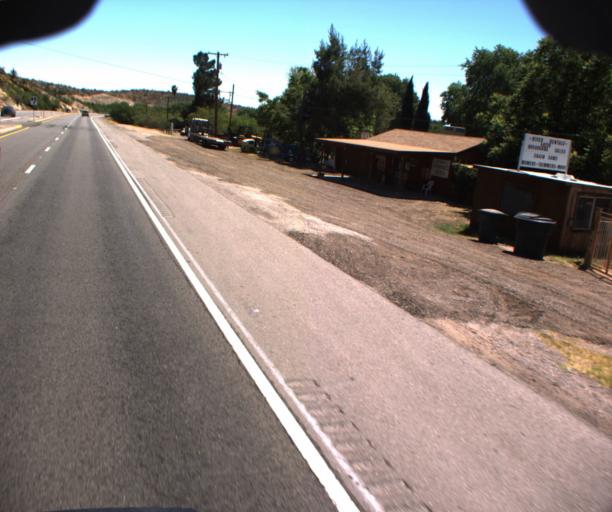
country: US
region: Arizona
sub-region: Maricopa County
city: Wickenburg
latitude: 33.9218
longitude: -112.6805
